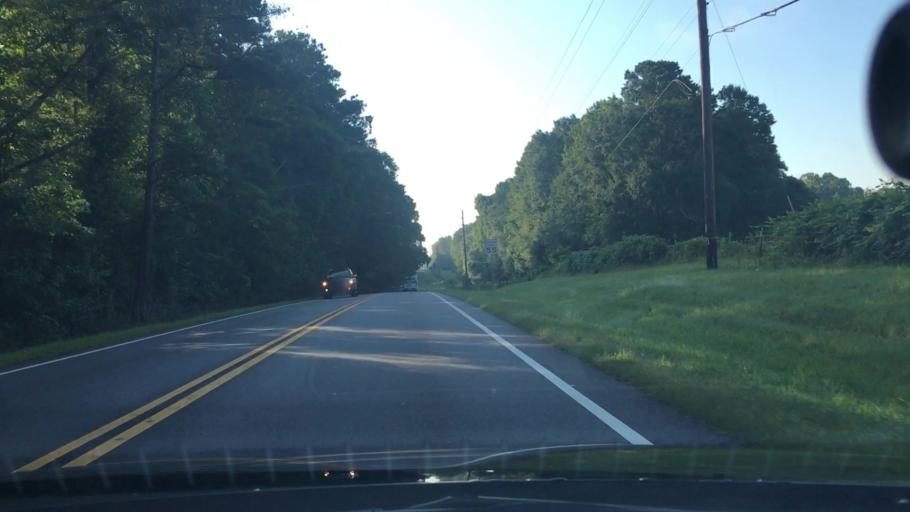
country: US
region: Georgia
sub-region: Coweta County
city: Senoia
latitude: 33.3225
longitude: -84.6283
